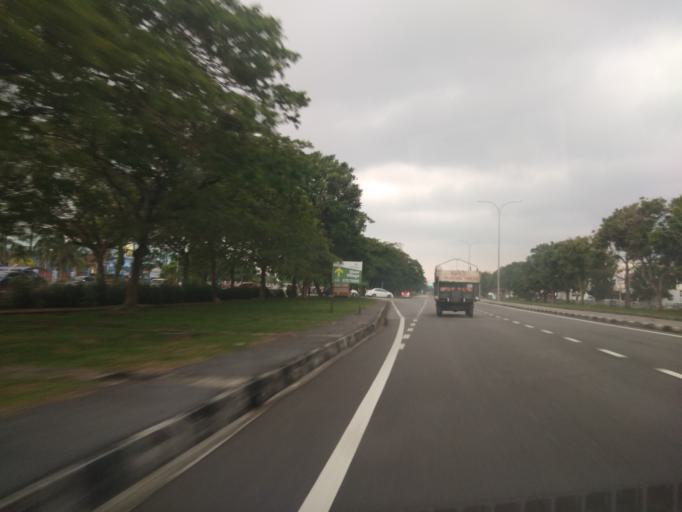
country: MY
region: Penang
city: Tasek Glugor
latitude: 5.5201
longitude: 100.4800
